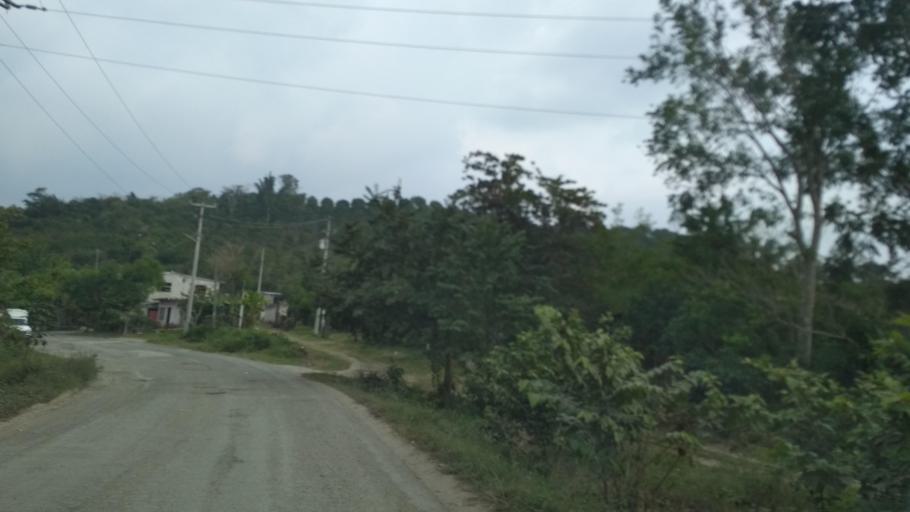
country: MM
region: Kayah
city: Loikaw
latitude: 20.2401
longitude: 97.2748
